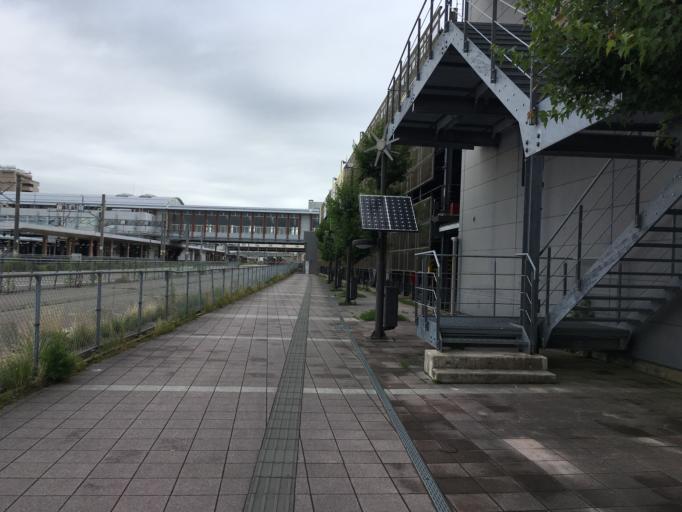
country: JP
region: Akita
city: Akita
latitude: 39.7153
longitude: 140.1305
